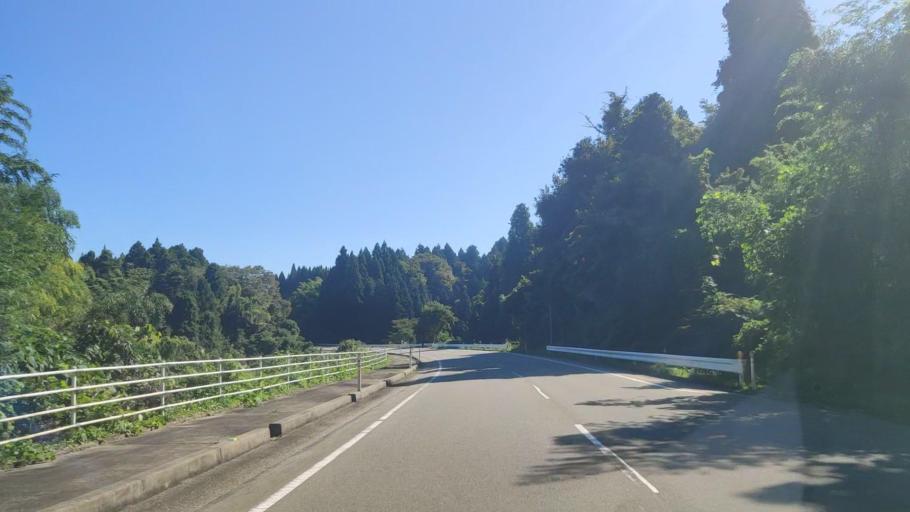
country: JP
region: Ishikawa
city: Nanao
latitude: 37.3785
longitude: 137.2335
